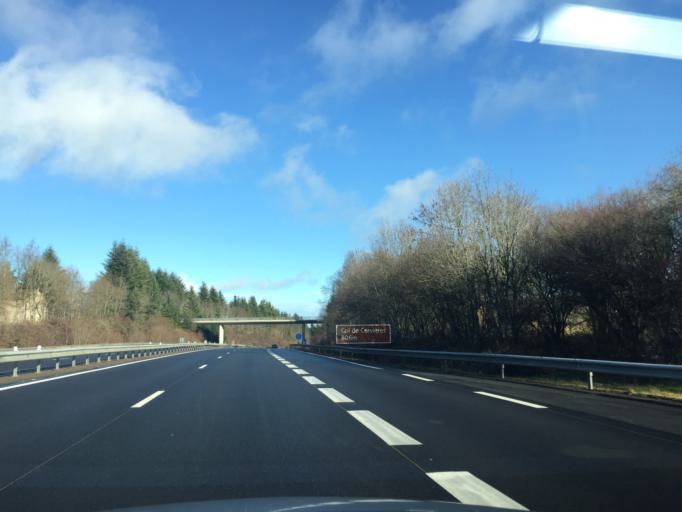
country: FR
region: Rhone-Alpes
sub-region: Departement de la Loire
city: Noiretable
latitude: 45.8489
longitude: 3.7645
